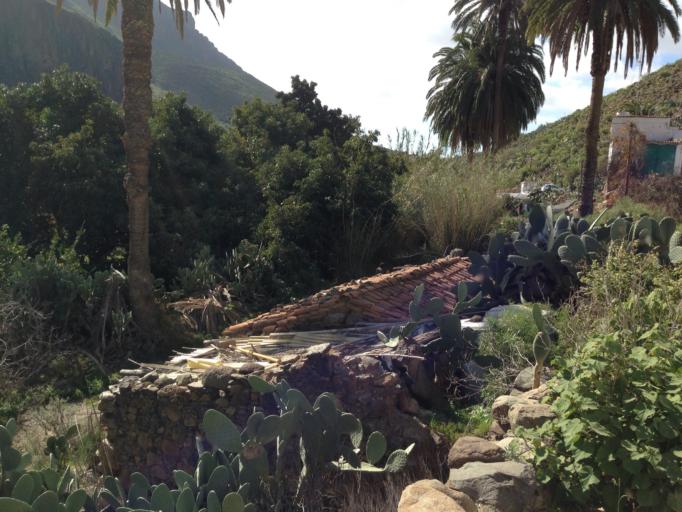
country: ES
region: Canary Islands
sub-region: Provincia de Las Palmas
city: Santa Lucia
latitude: 27.8483
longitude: -15.5679
